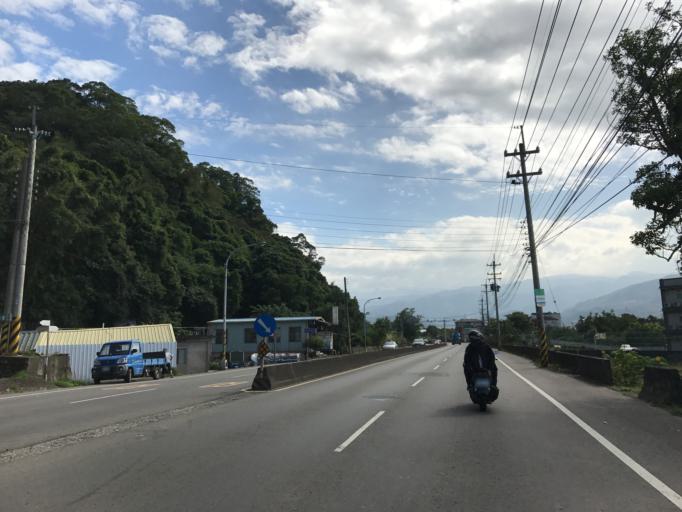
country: TW
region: Taiwan
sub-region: Hsinchu
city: Zhubei
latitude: 24.7396
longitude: 121.1108
